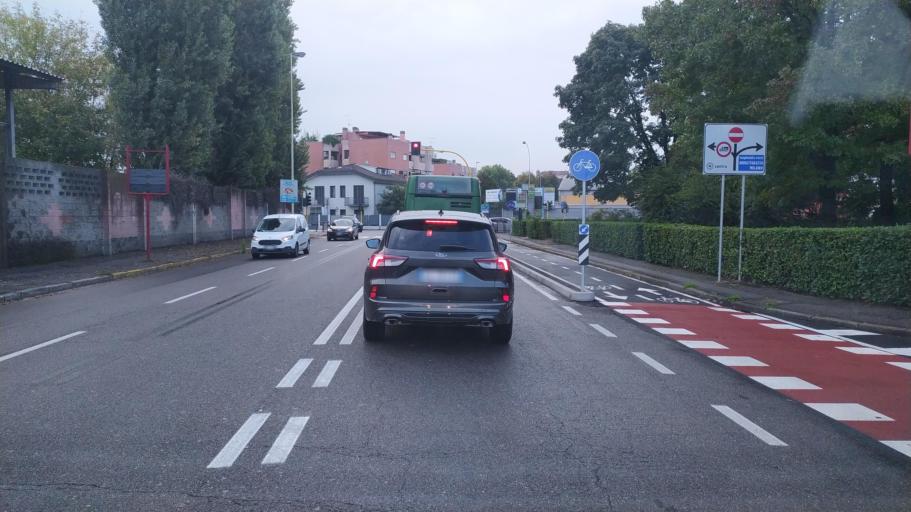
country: IT
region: Lombardy
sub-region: Citta metropolitana di Milano
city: Trezzano sul Naviglio
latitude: 45.4293
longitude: 9.0549
